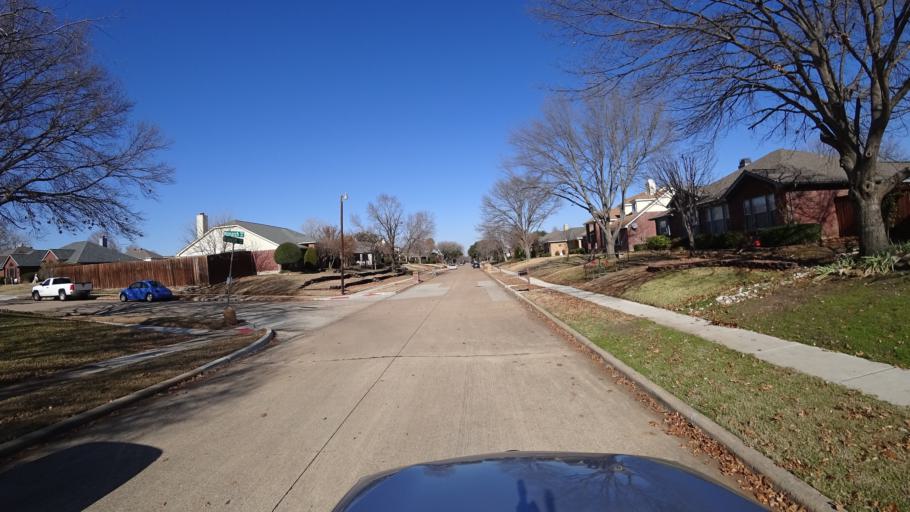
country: US
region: Texas
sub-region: Denton County
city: Lewisville
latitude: 33.0091
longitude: -97.0158
